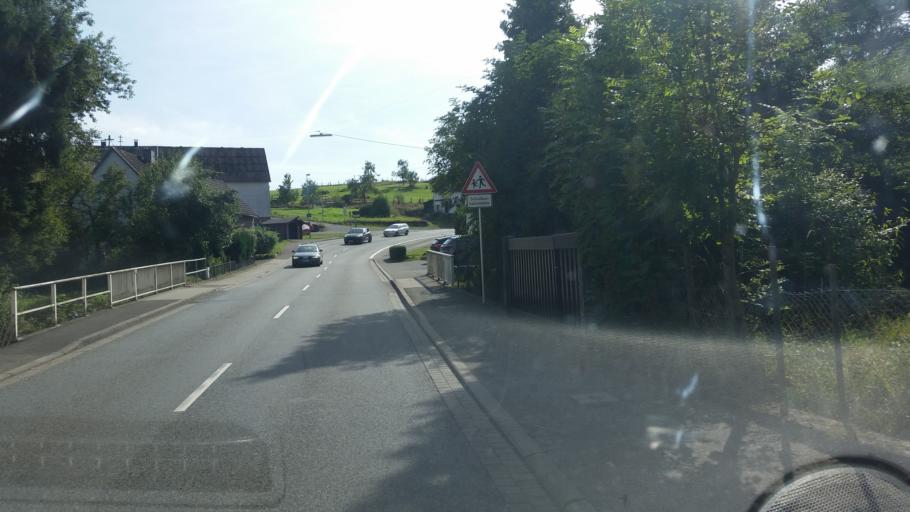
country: DE
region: Rheinland-Pfalz
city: Kaden
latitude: 50.5636
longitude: 7.9004
